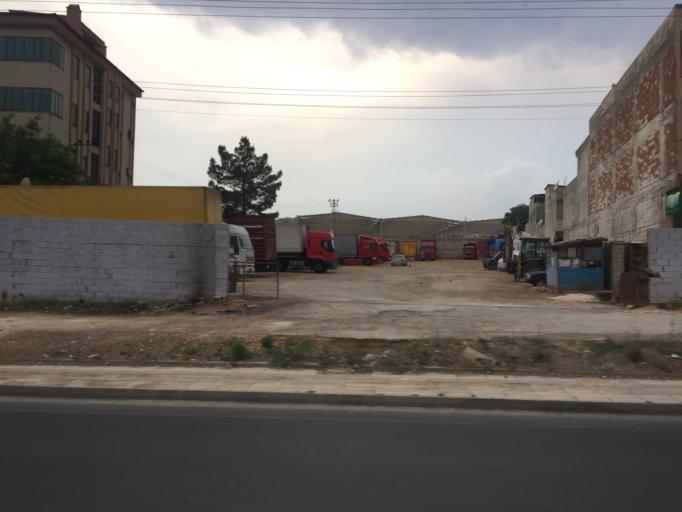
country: TR
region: Gaziantep
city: Gaziantep
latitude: 37.0400
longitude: 37.4239
